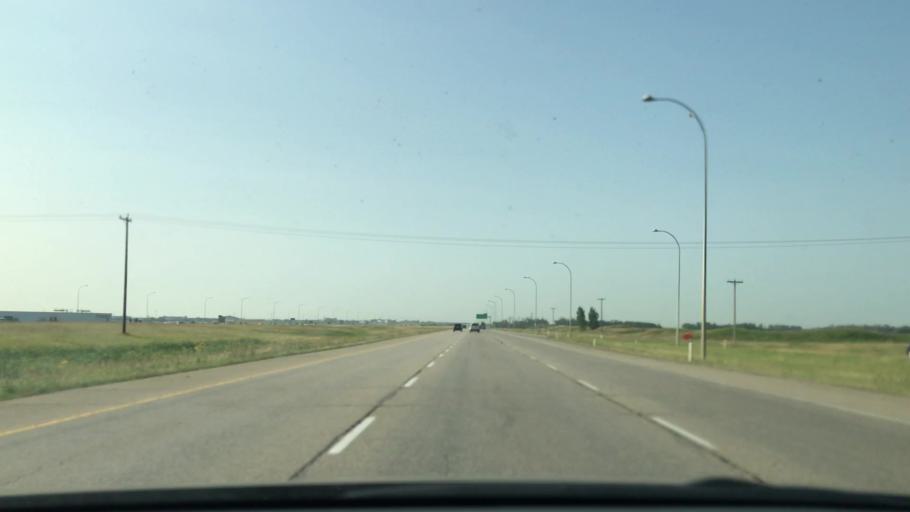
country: CA
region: Alberta
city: Leduc
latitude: 53.3356
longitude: -113.5496
